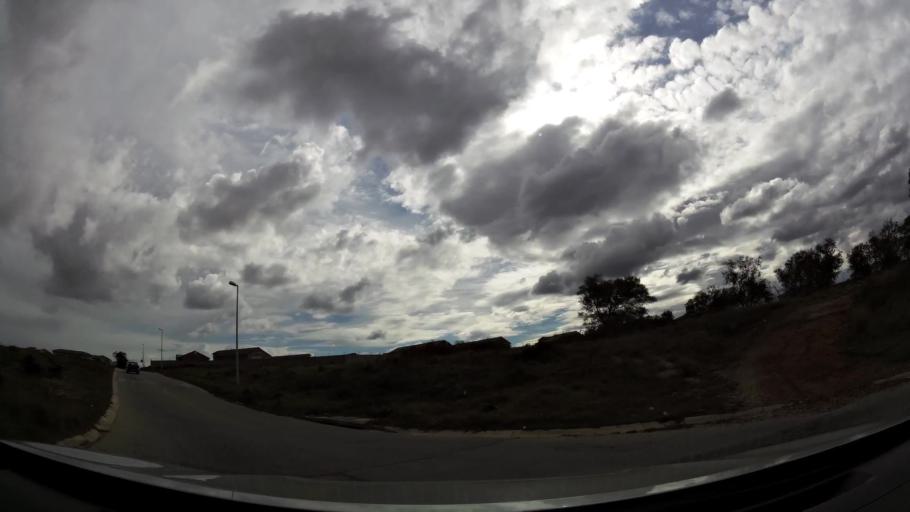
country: ZA
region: Eastern Cape
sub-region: Nelson Mandela Bay Metropolitan Municipality
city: Port Elizabeth
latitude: -33.9317
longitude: 25.5066
